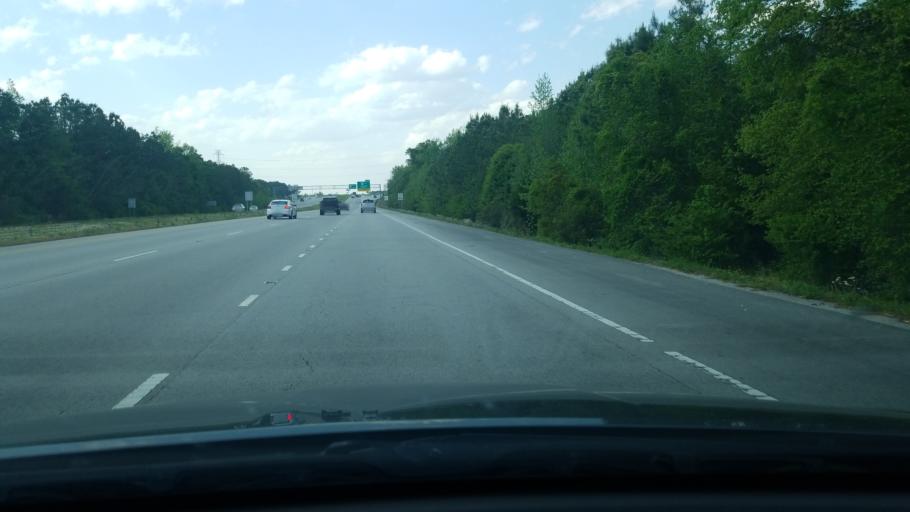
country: US
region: North Carolina
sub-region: Onslow County
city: Jacksonville
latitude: 34.7621
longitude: -77.3946
